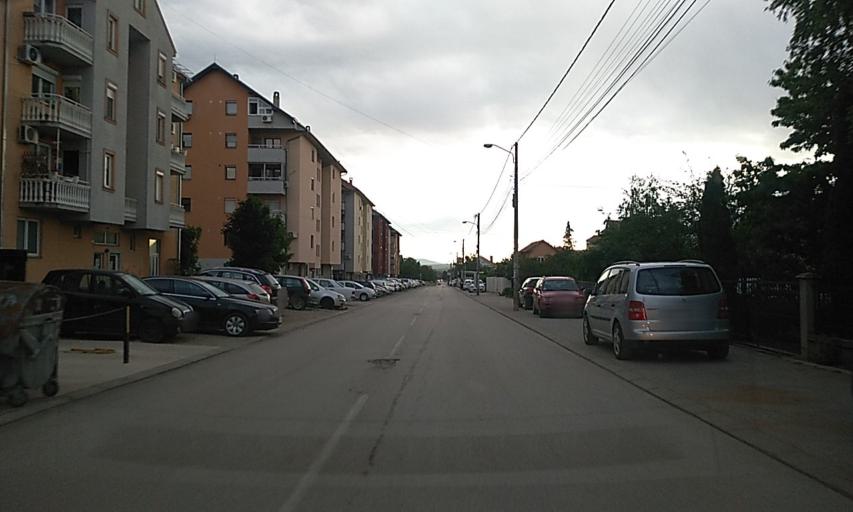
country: RS
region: Central Serbia
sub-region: Nisavski Okrug
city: Nis
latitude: 43.3392
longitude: 21.9230
